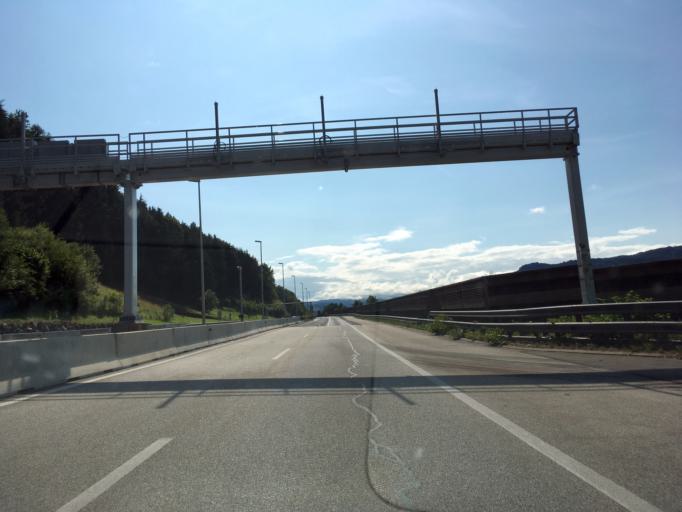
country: AT
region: Styria
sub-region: Politischer Bezirk Leoben
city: Niklasdorf
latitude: 47.3878
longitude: 15.1520
